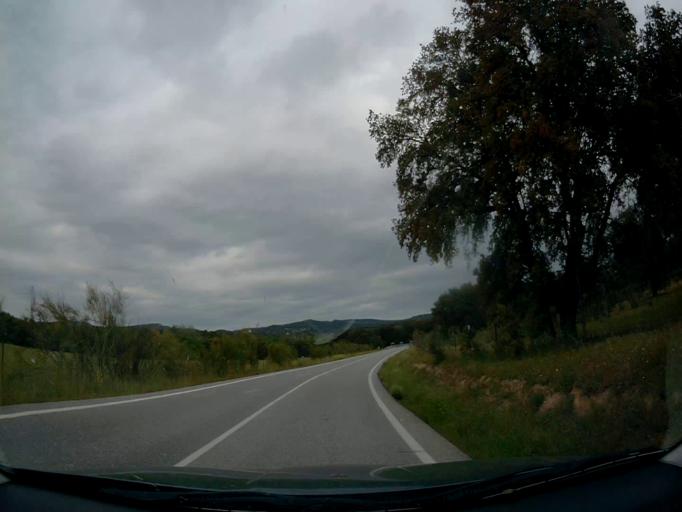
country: ES
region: Madrid
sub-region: Provincia de Madrid
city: Quijorna
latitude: 40.4206
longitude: -4.0910
